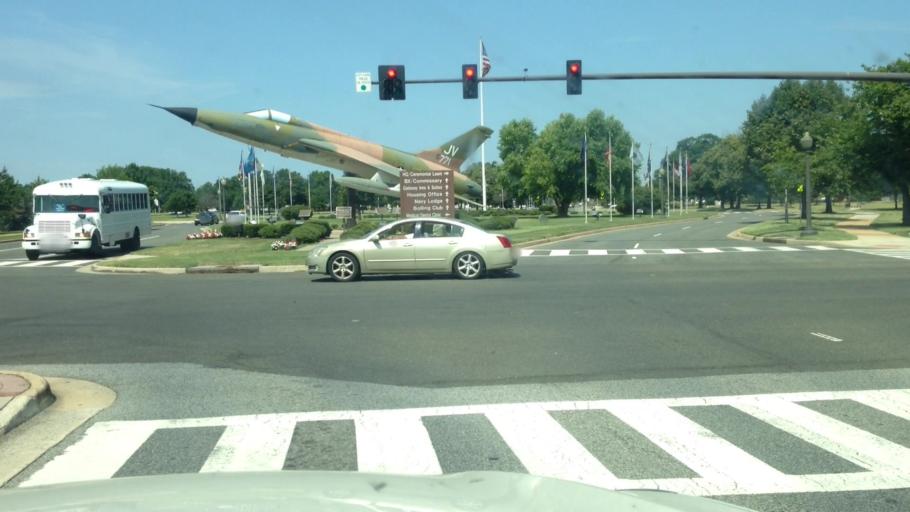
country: US
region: Maryland
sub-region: Prince George's County
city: Glassmanor
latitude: 38.8451
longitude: -77.0111
